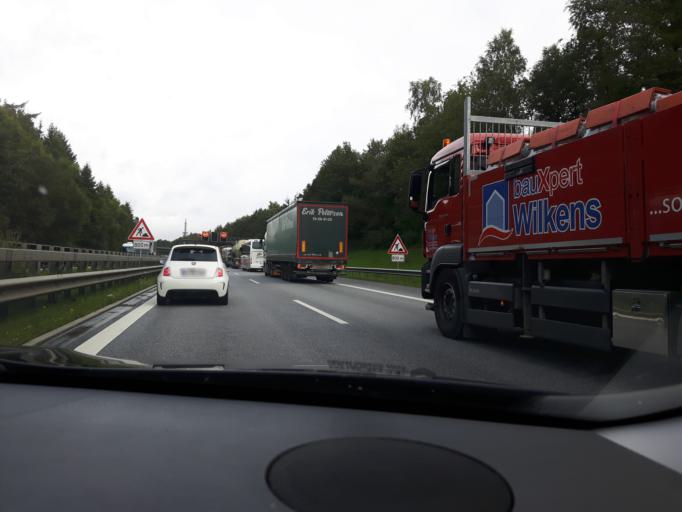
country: DE
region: Lower Saxony
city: Seevetal
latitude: 53.4278
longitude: 9.9282
